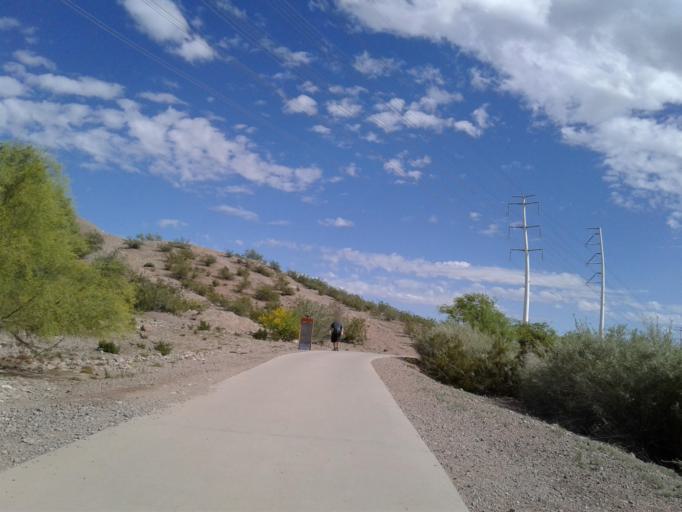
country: US
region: Arizona
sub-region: Maricopa County
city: Tempe Junction
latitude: 33.4451
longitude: -111.9400
